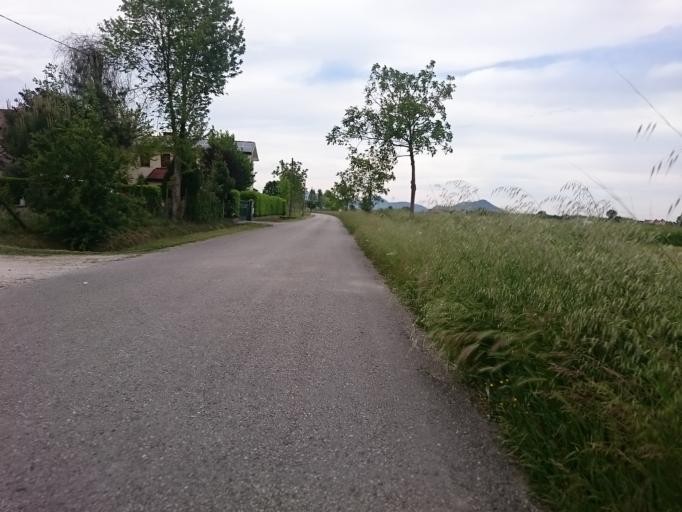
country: IT
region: Veneto
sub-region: Provincia di Padova
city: Sant'Elena
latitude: 45.1771
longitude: 11.7227
